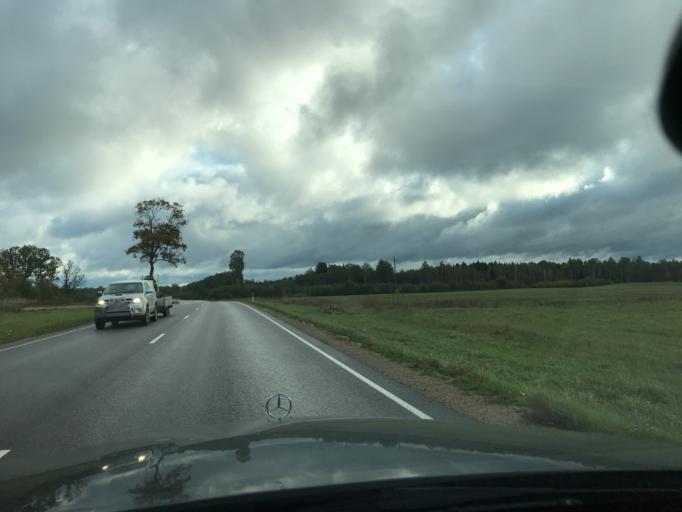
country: EE
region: Valgamaa
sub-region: Torva linn
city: Torva
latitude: 58.0094
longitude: 25.7815
